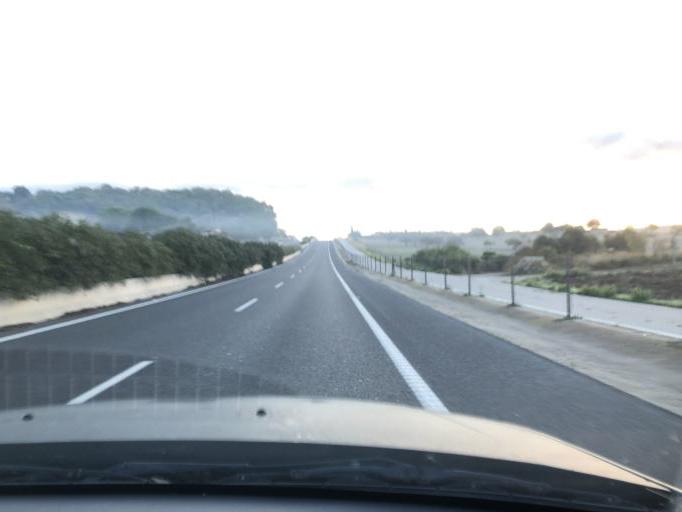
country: ES
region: Balearic Islands
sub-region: Illes Balears
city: Montuiri
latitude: 39.5612
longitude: 3.0173
